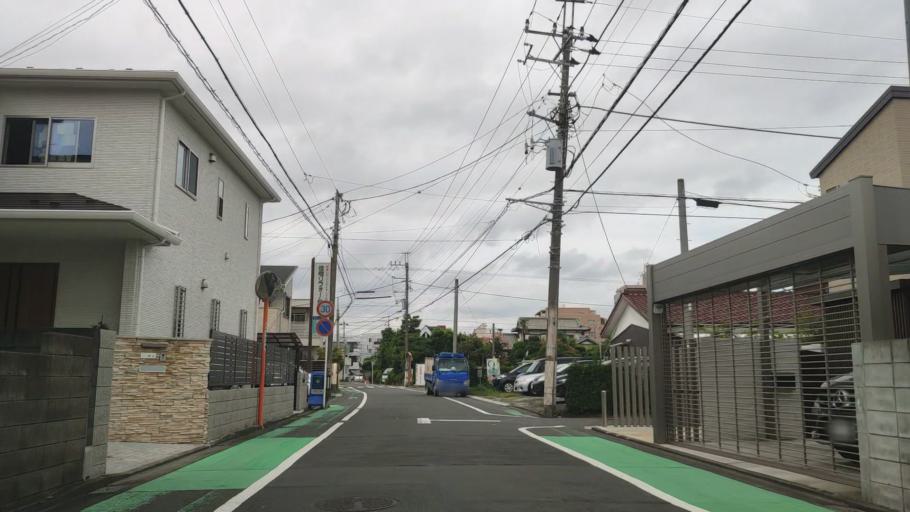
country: JP
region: Tokyo
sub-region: Machida-shi
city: Machida
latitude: 35.5173
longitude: 139.4352
